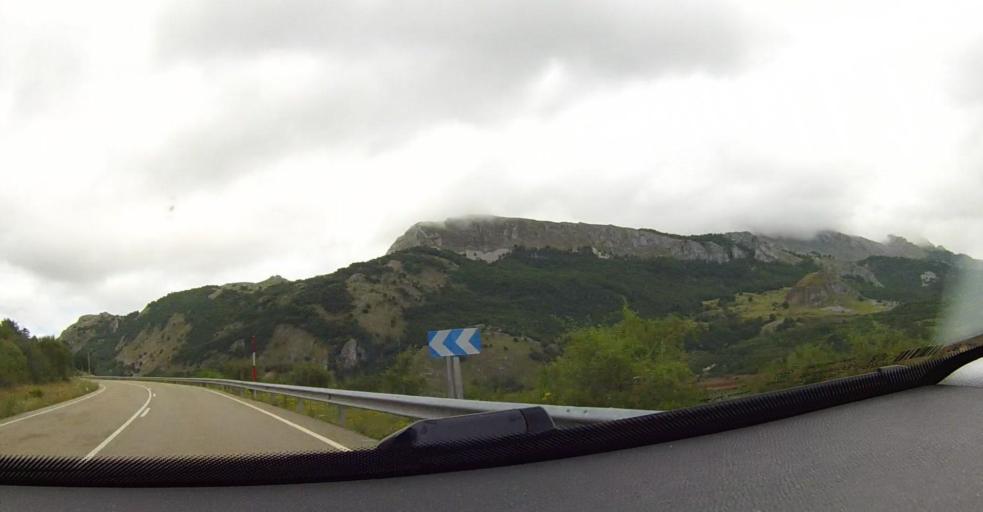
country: ES
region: Castille and Leon
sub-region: Provincia de Leon
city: Buron
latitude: 43.0195
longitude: -5.0357
